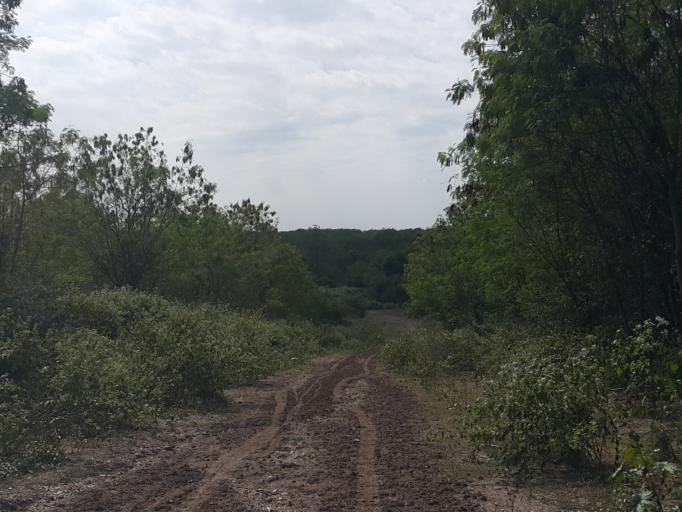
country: TH
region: Lampang
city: Mae Mo
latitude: 18.3407
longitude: 99.7650
